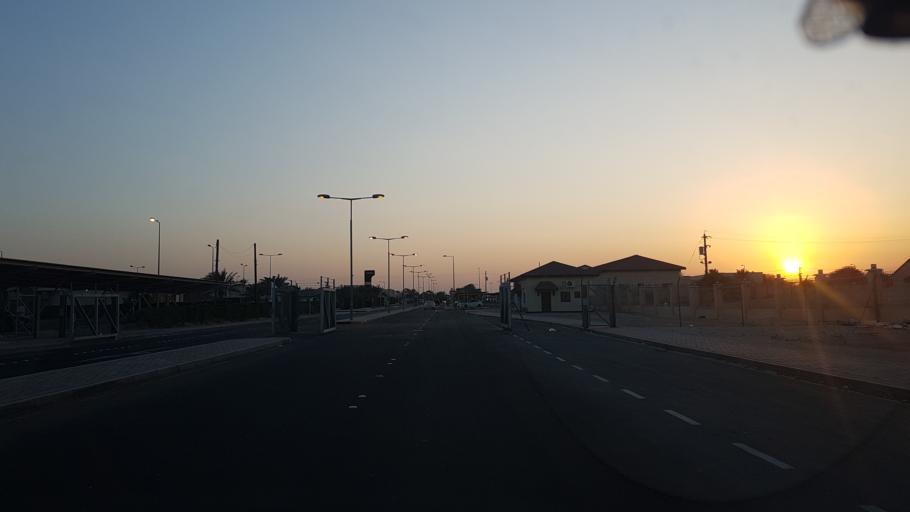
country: BH
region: Northern
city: Ar Rifa'
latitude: 26.0898
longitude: 50.5522
